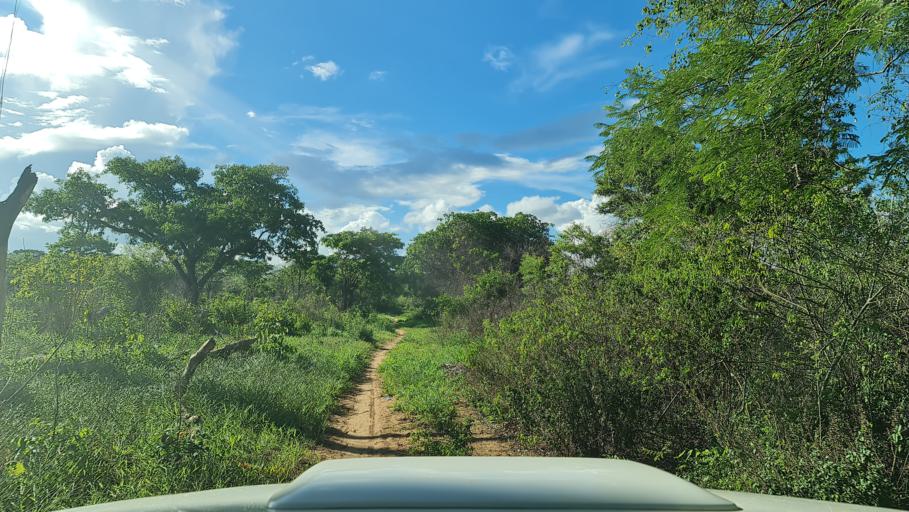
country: MZ
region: Nampula
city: Ilha de Mocambique
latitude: -15.2490
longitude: 40.1804
